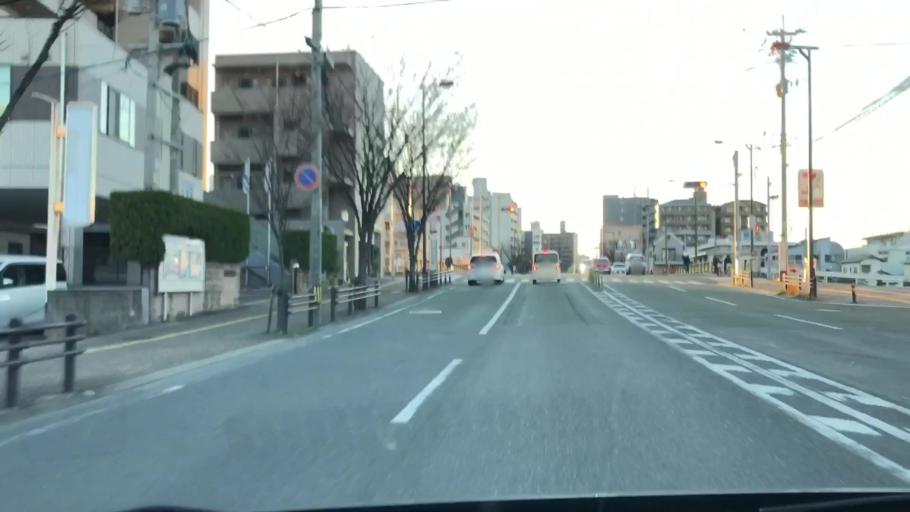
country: JP
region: Fukuoka
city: Fukuoka-shi
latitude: 33.6190
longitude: 130.4310
